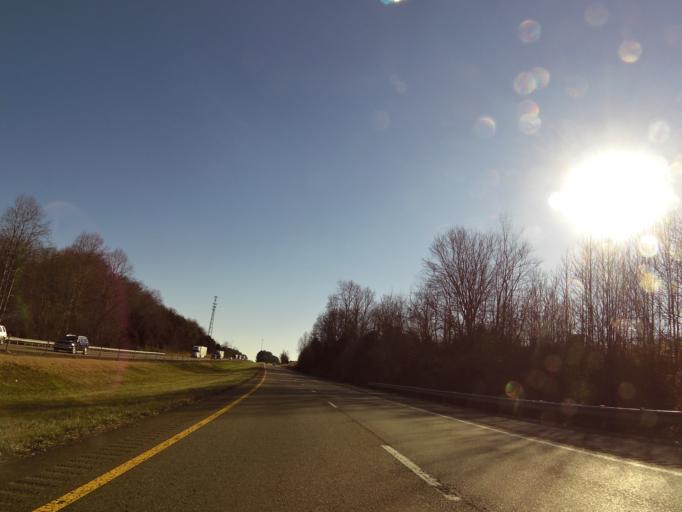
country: US
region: Tennessee
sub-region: Cocke County
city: Newport
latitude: 35.9730
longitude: -83.2687
